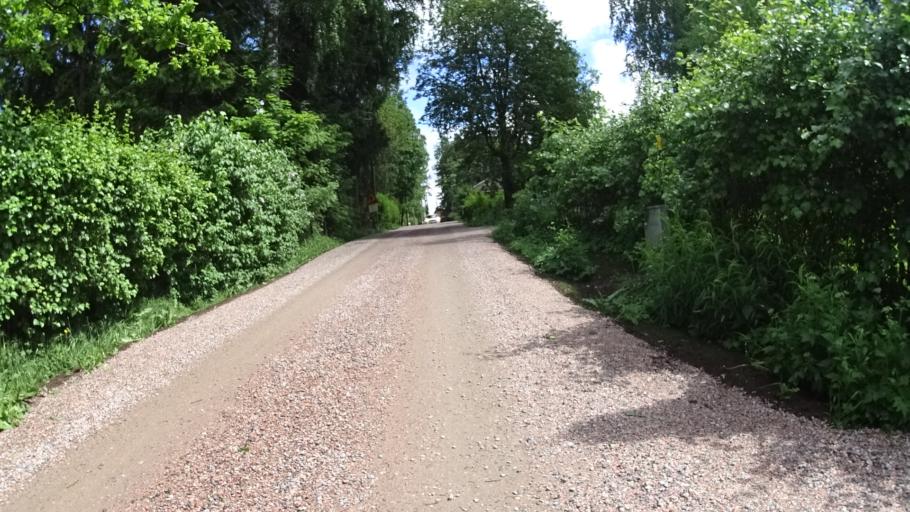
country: FI
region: Uusimaa
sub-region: Helsinki
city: Kilo
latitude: 60.2411
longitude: 24.8142
